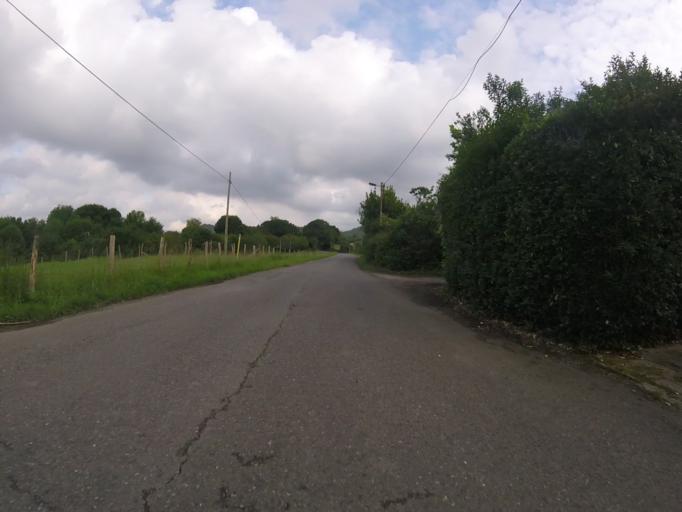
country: ES
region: Basque Country
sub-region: Provincia de Guipuzcoa
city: Pasaia
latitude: 43.3046
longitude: -1.9363
